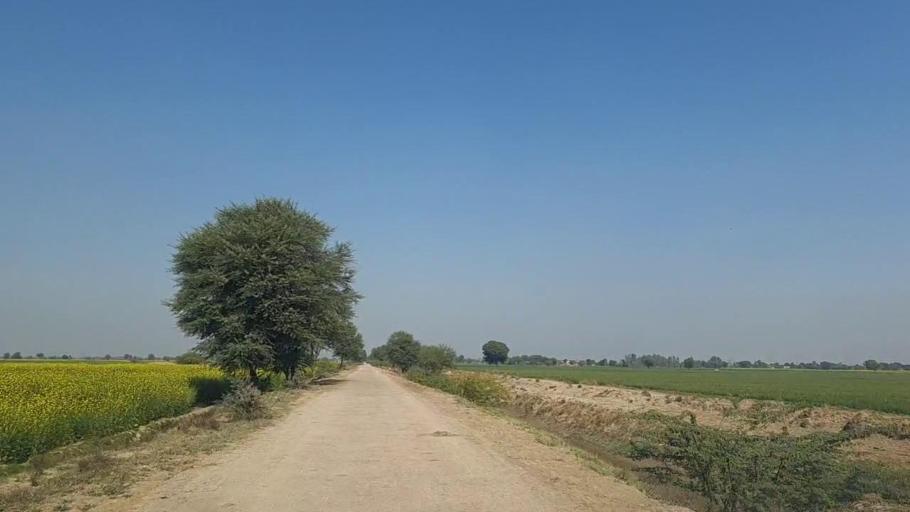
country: PK
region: Sindh
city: Shahpur Chakar
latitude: 26.1843
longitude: 68.6017
